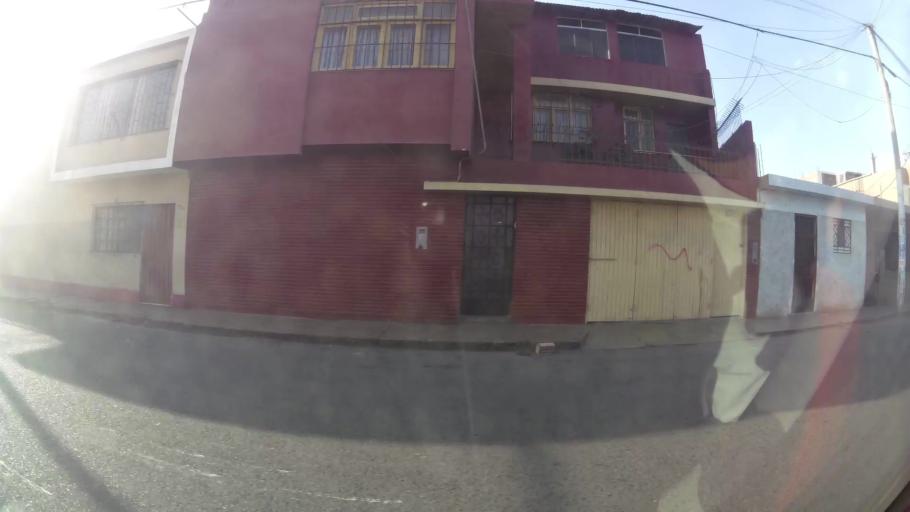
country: PE
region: Lima
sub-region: Huaura
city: Huacho
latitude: -11.1102
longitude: -77.6062
